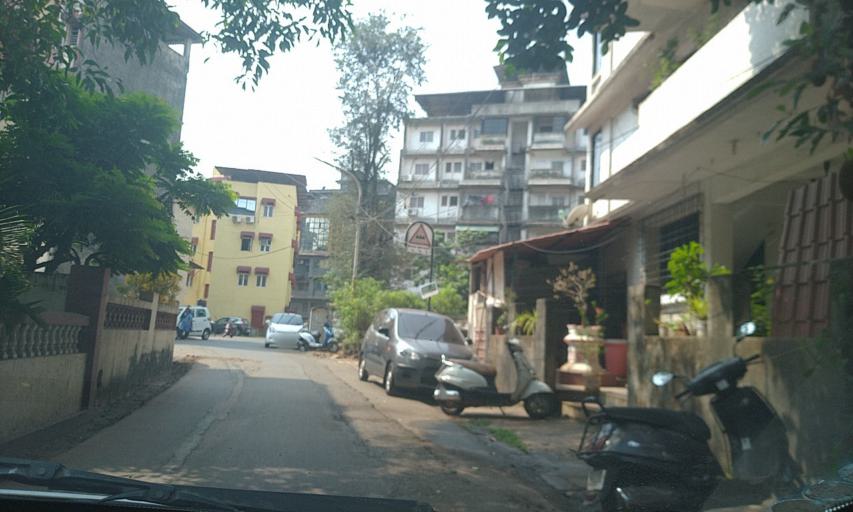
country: IN
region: Goa
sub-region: North Goa
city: Panaji
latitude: 15.4939
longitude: 73.8213
